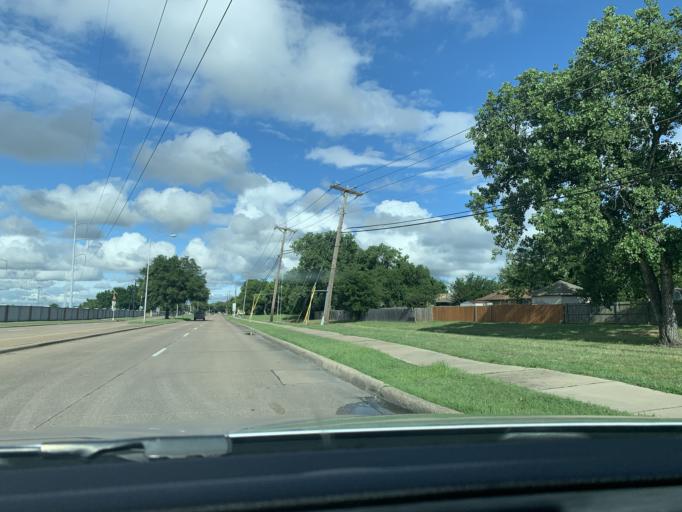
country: US
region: Texas
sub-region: Dallas County
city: Grand Prairie
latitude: 32.6582
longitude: -97.0216
